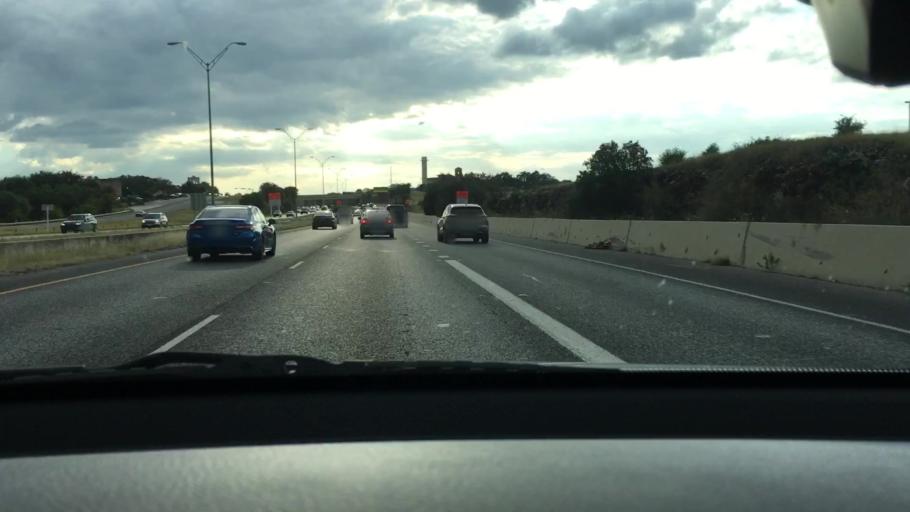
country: US
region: Texas
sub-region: Bexar County
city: Hollywood Park
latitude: 29.6094
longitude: -98.5163
